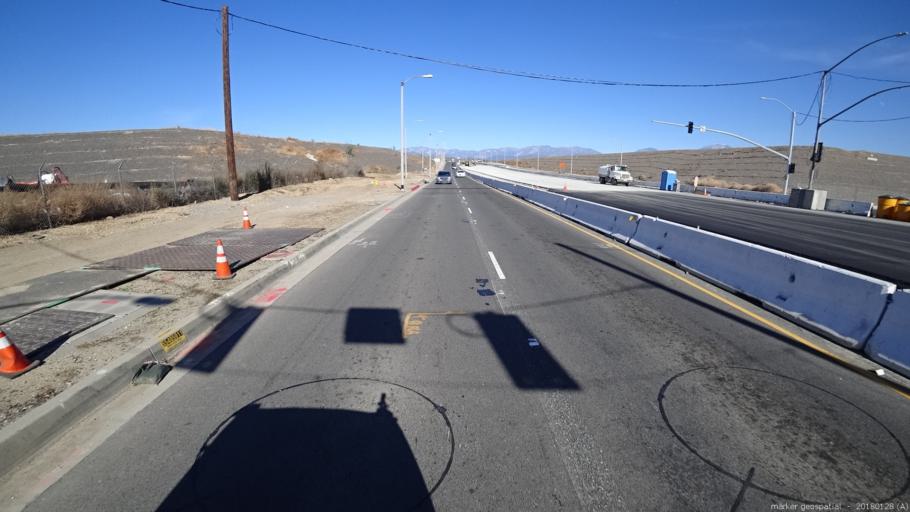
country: US
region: California
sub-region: Los Angeles County
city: Diamond Bar
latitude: 34.0125
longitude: -117.8240
